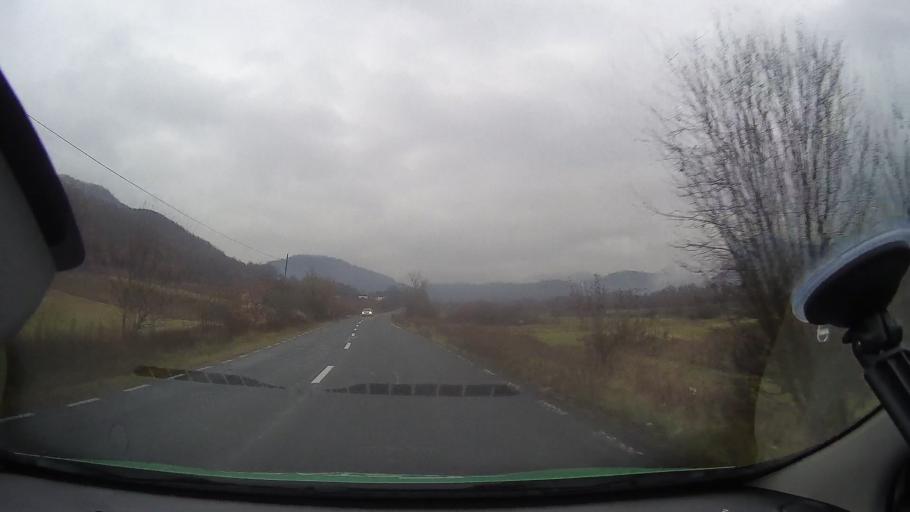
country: RO
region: Arad
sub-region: Comuna Plescuta
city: Plescuta
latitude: 46.2975
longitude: 22.4284
